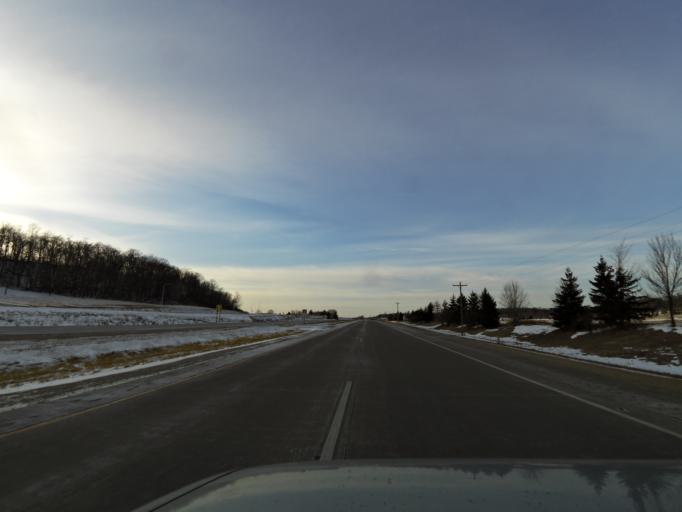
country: US
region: Wisconsin
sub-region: Pierce County
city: River Falls
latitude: 44.8927
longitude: -92.6376
